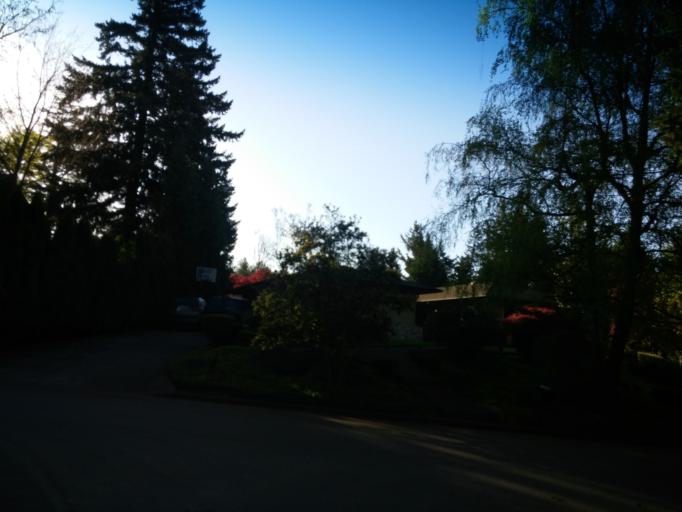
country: US
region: Oregon
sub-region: Washington County
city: Cedar Hills
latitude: 45.5108
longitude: -122.7929
